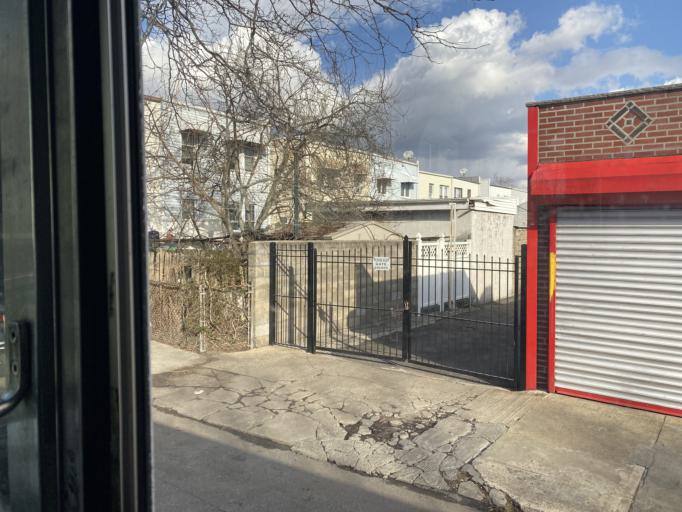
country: US
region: New York
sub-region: Kings County
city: East New York
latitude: 40.7157
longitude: -73.9034
